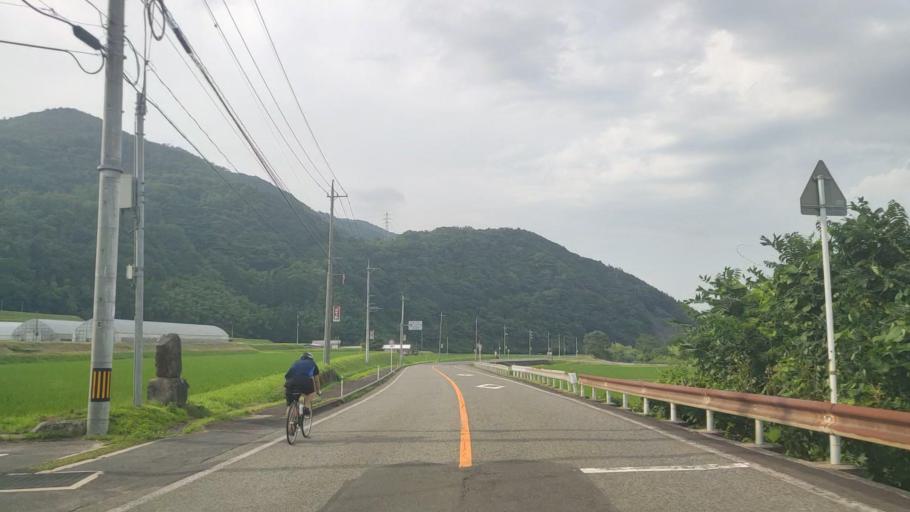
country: JP
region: Tottori
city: Kurayoshi
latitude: 35.3584
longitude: 133.8460
